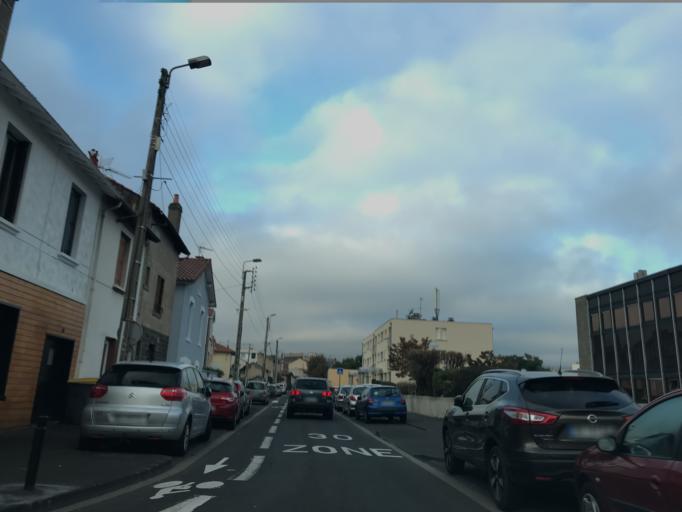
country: FR
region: Auvergne
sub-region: Departement du Puy-de-Dome
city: Clermont-Ferrand
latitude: 45.7967
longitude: 3.1164
